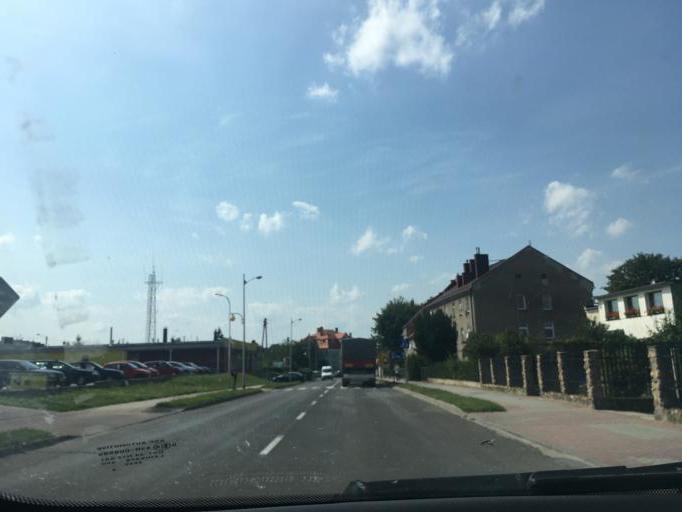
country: PL
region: Opole Voivodeship
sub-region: Powiat glubczycki
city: Glubczyce
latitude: 50.1954
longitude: 17.8350
